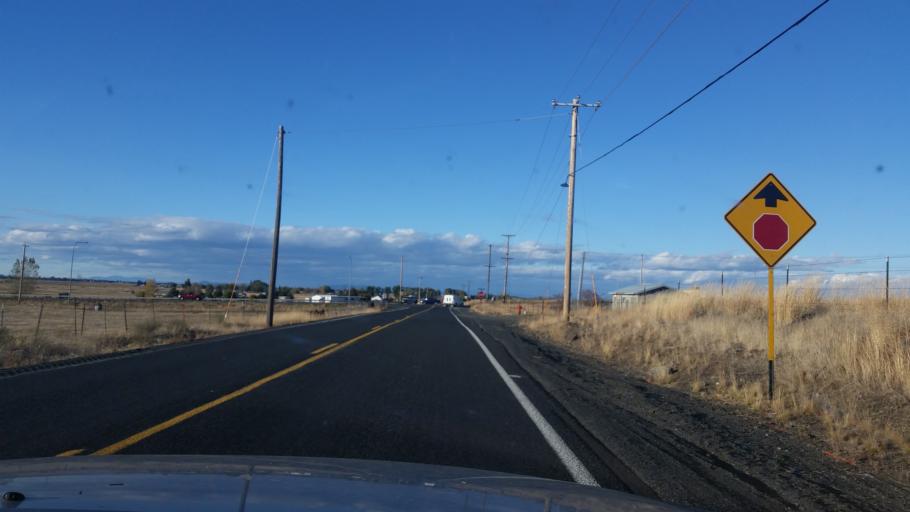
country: US
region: Washington
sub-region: Spokane County
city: Fairchild Air Force Base
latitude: 47.5930
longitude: -117.6075
